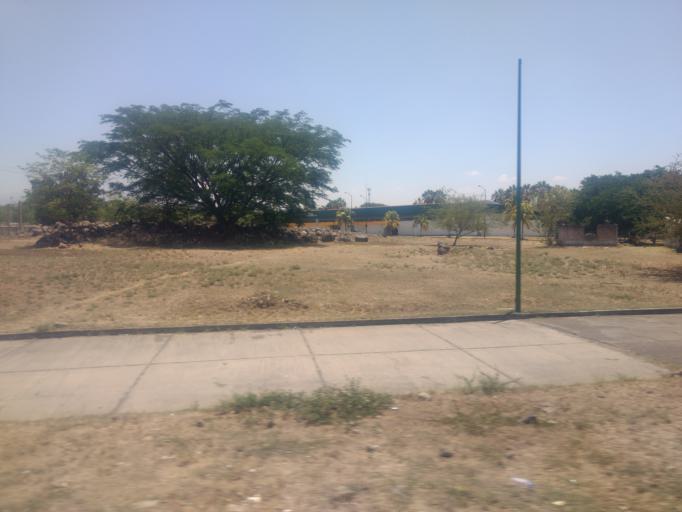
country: MX
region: Colima
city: Colima
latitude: 19.2314
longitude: -103.7052
